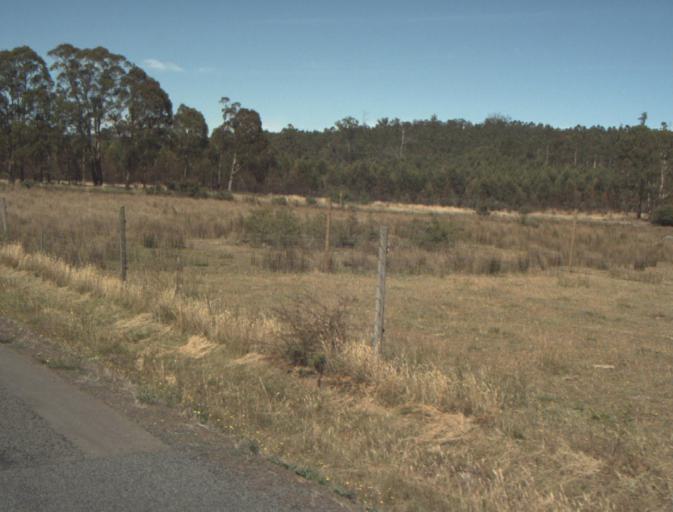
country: AU
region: Tasmania
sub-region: Launceston
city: Newstead
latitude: -41.3782
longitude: 147.2967
